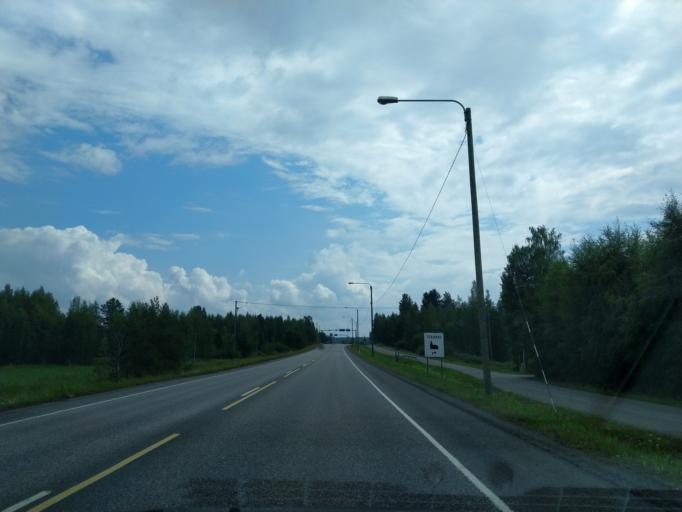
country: FI
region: South Karelia
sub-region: Imatra
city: Parikkala
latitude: 61.5894
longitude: 29.4904
